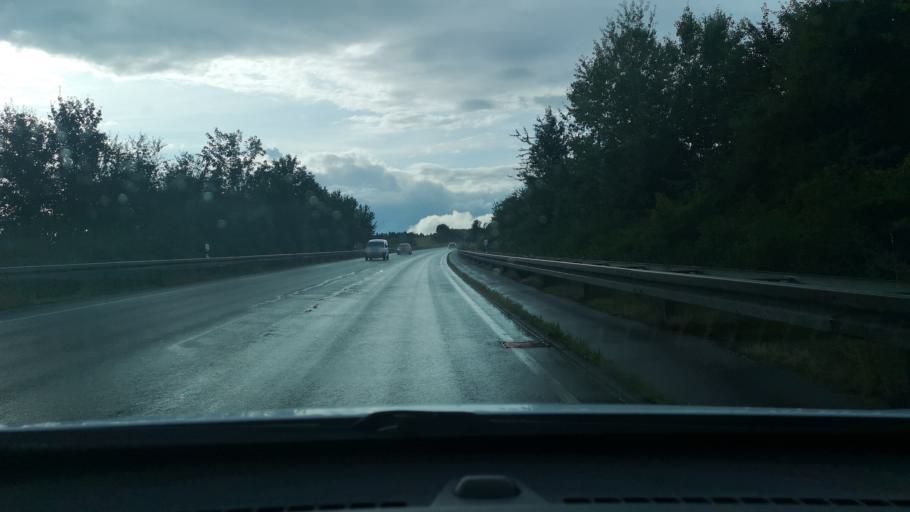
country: DE
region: Baden-Wuerttemberg
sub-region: Freiburg Region
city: Zimmern ob Rottweil
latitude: 48.1512
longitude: 8.6092
